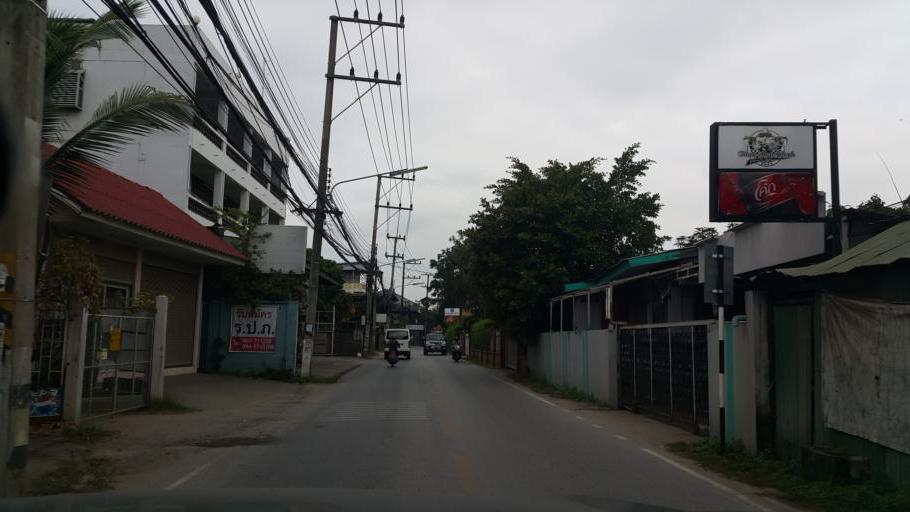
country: TH
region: Chiang Mai
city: Chiang Mai
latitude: 18.8028
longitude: 99.0030
